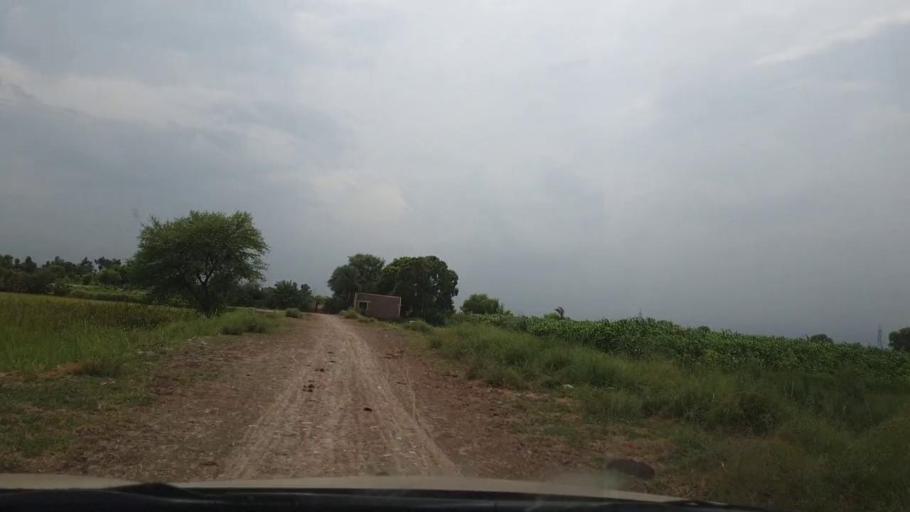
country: PK
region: Sindh
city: Ratodero
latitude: 27.7961
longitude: 68.3121
